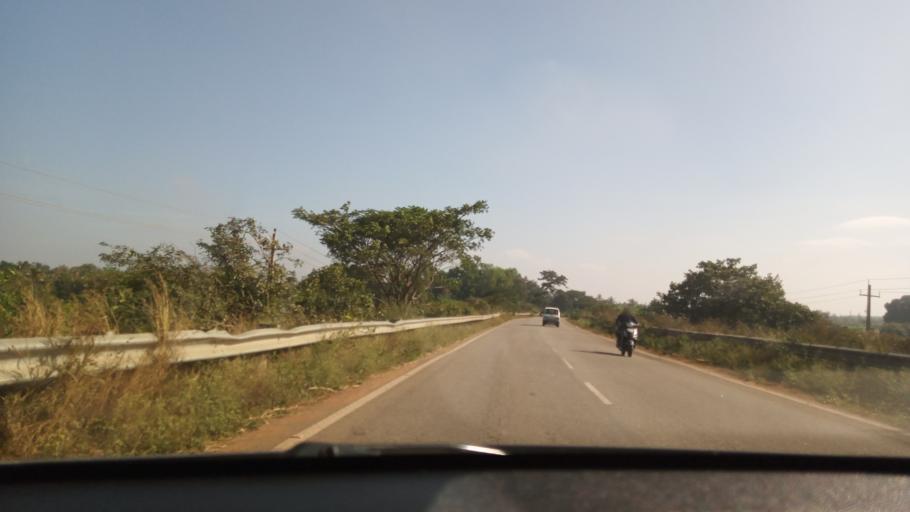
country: IN
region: Karnataka
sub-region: Bangalore Rural
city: Vijayapura
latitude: 13.2786
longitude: 77.7601
